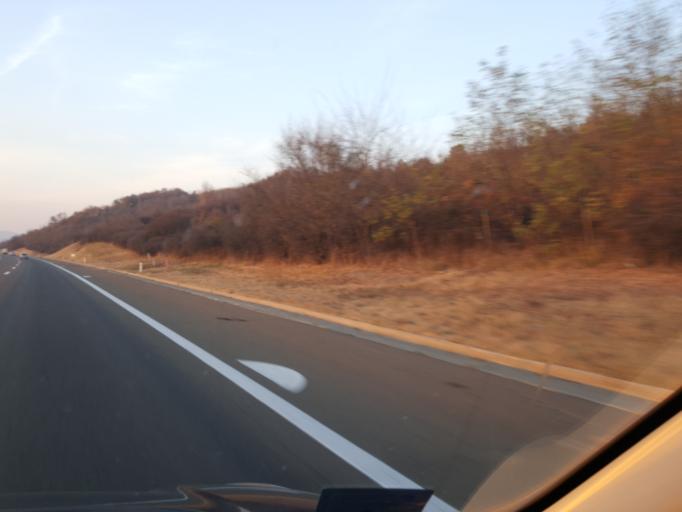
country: RS
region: Central Serbia
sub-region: Nisavski Okrug
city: Aleksinac
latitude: 43.4682
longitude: 21.7821
